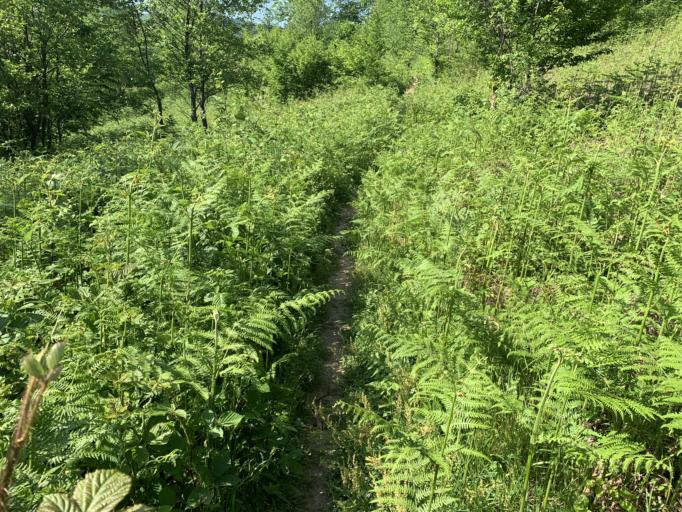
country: RU
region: Krasnodarskiy
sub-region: Sochi City
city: Lazarevskoye
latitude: 43.9518
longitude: 39.3227
